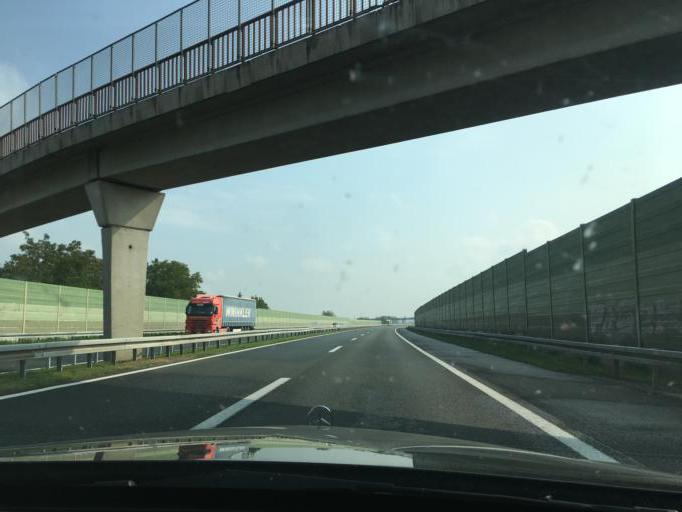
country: HR
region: Brodsko-Posavska
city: Podvinje
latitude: 45.1844
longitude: 18.0241
